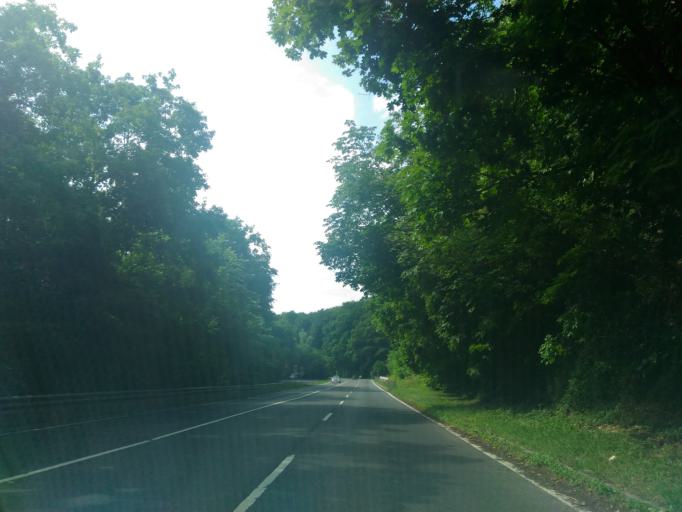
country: HU
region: Baranya
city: Komlo
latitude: 46.1441
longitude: 18.2494
